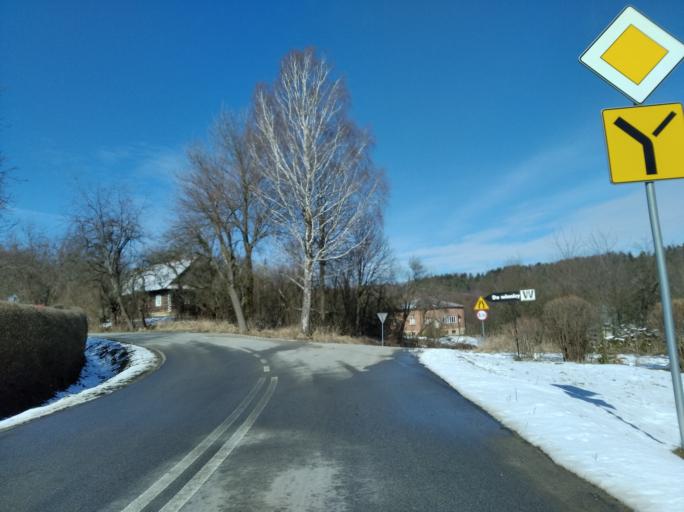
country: PL
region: Subcarpathian Voivodeship
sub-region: Powiat brzozowski
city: Jablonica Polska
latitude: 49.7253
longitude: 21.8773
